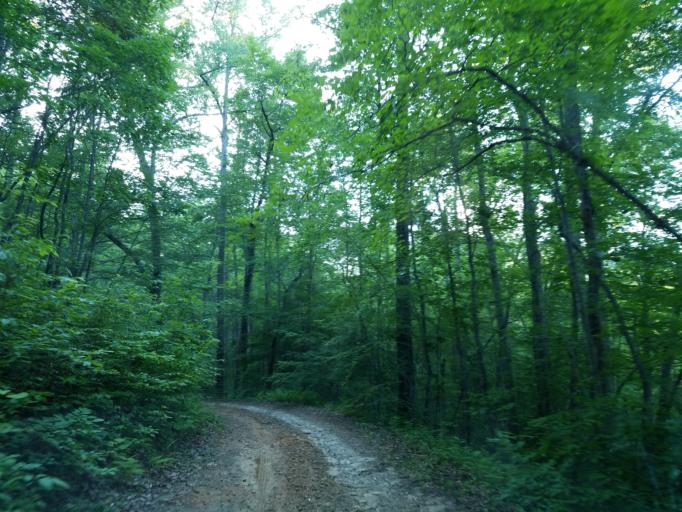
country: US
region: Georgia
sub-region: Fannin County
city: Blue Ridge
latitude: 34.8126
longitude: -84.1585
